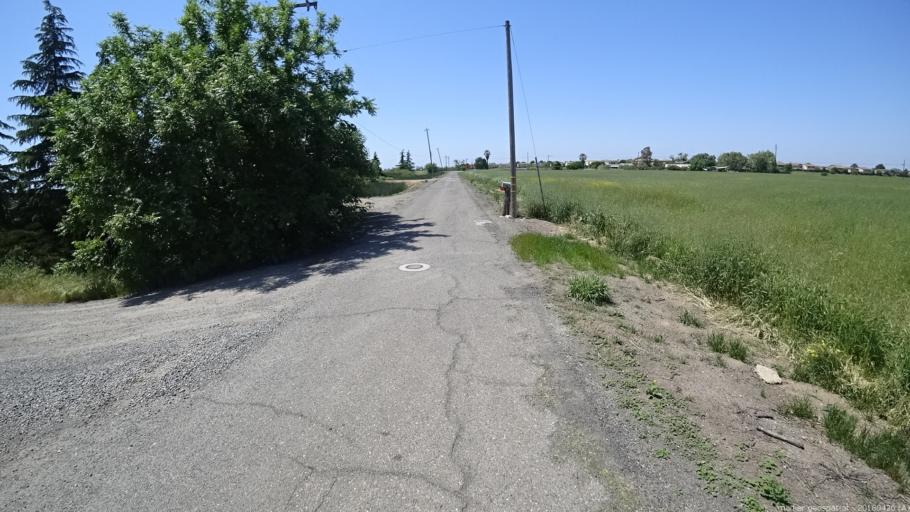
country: US
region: California
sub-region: Yolo County
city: West Sacramento
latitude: 38.5235
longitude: -121.5617
